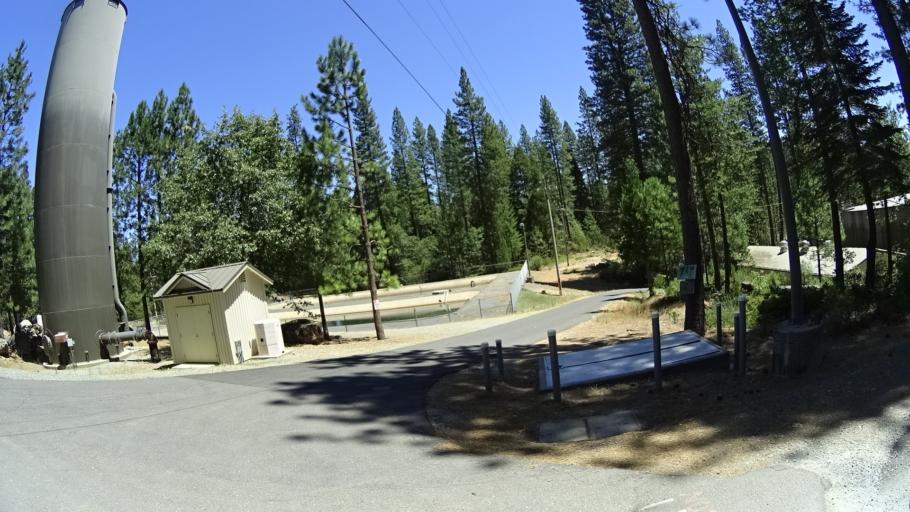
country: US
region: California
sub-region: Calaveras County
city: Forest Meadows
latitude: 38.1983
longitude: -120.3630
